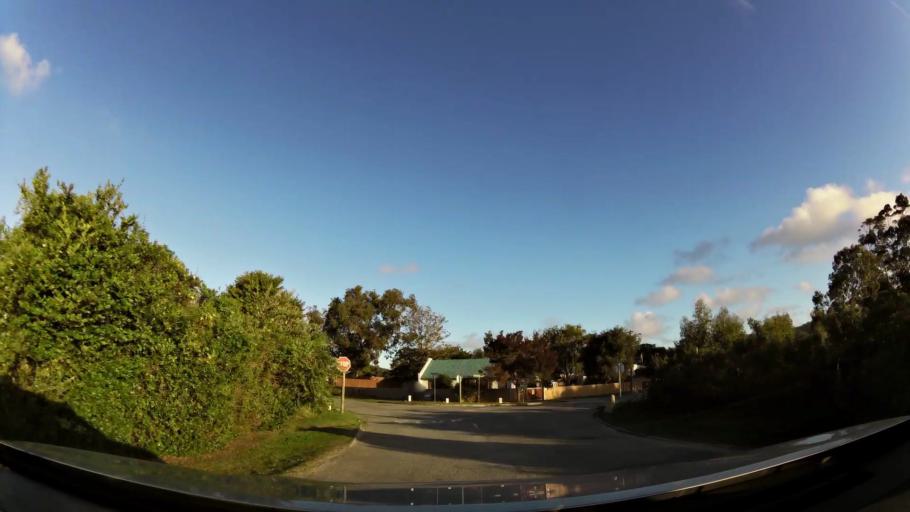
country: ZA
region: Western Cape
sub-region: Eden District Municipality
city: Knysna
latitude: -34.0122
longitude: 22.7795
